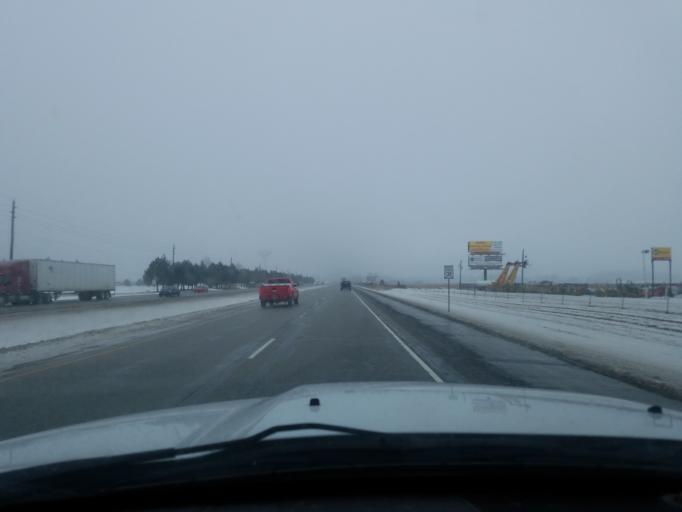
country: US
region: Indiana
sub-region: Miami County
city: Grissom Air Force Base
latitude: 40.6431
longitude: -86.1275
